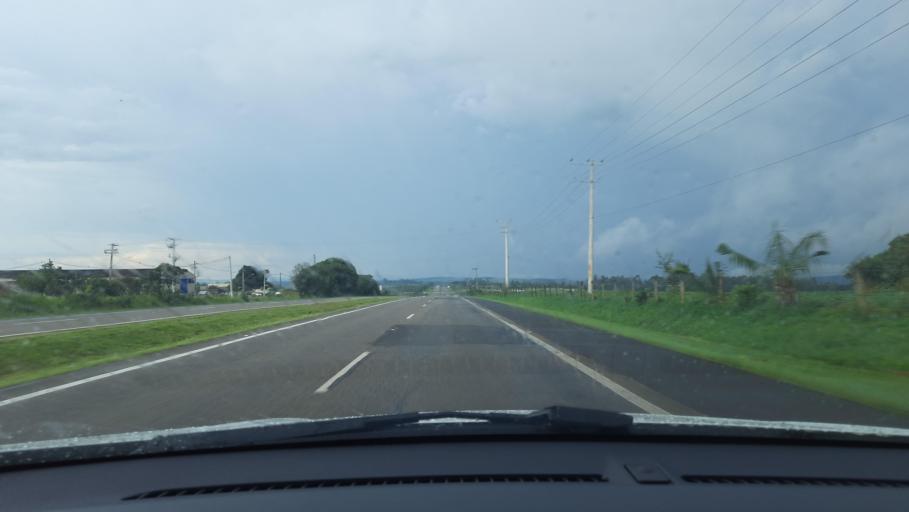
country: BR
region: Sao Paulo
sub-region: Casa Branca
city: Casa Branca
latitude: -21.7577
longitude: -47.0704
